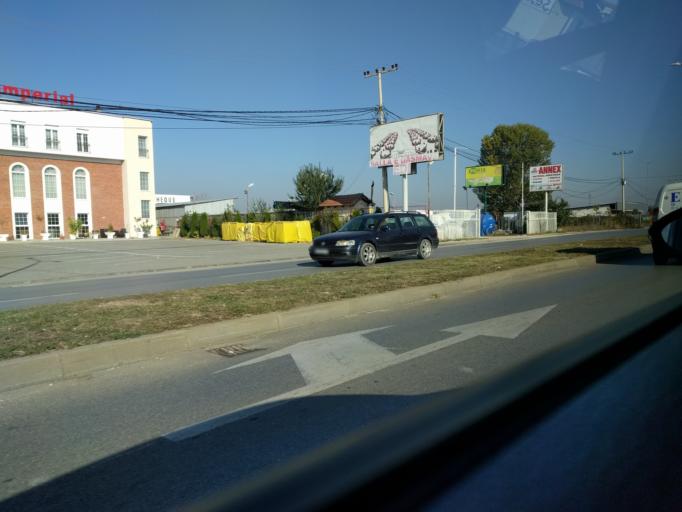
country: XK
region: Prizren
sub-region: Prizren
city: Prizren
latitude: 42.2329
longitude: 20.7578
